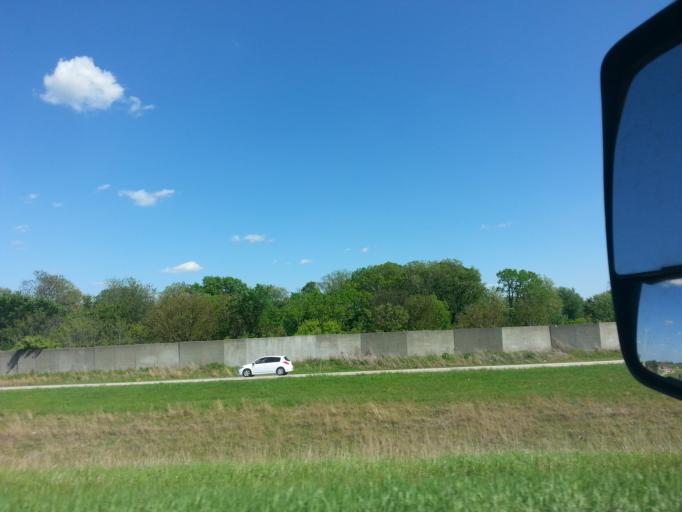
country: US
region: Illinois
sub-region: Winnebago County
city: Cherry Valley
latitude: 42.2191
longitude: -89.0080
